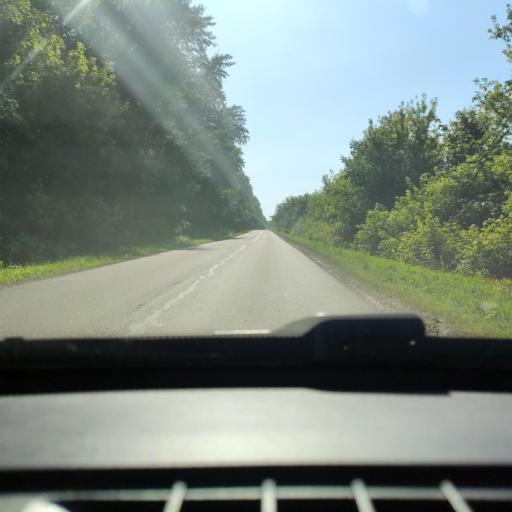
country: RU
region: Voronezj
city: Panino
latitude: 51.6176
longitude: 40.2201
